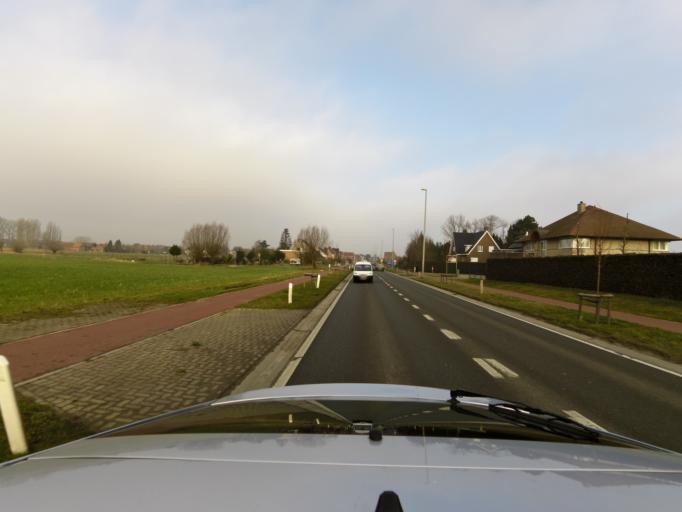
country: BE
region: Flanders
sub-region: Provincie West-Vlaanderen
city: Torhout
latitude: 51.0578
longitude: 3.0984
